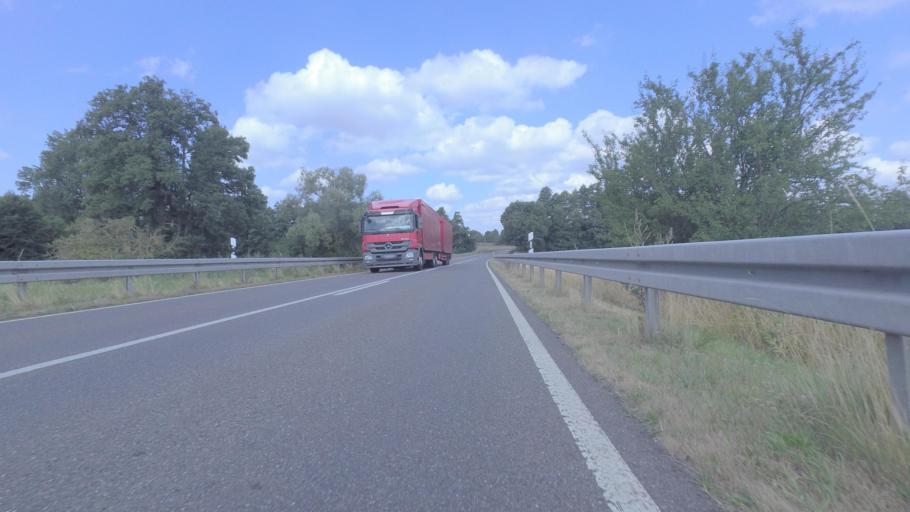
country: DE
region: Brandenburg
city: Walsleben
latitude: 52.9959
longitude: 12.6497
